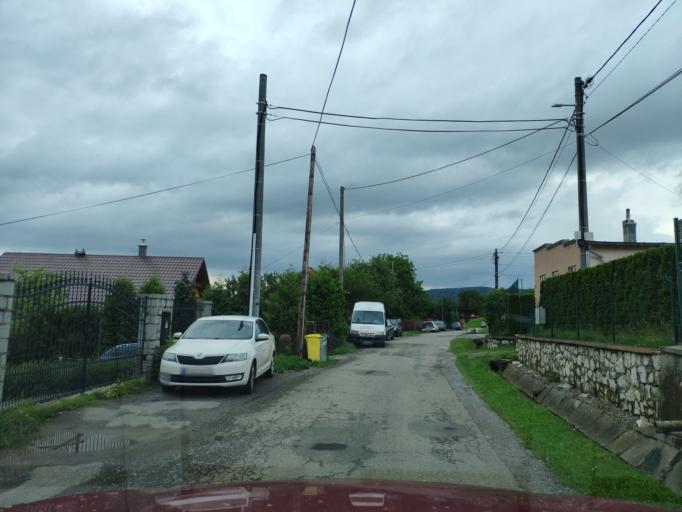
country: SK
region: Presovsky
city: Sabinov
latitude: 49.0444
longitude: 21.0151
